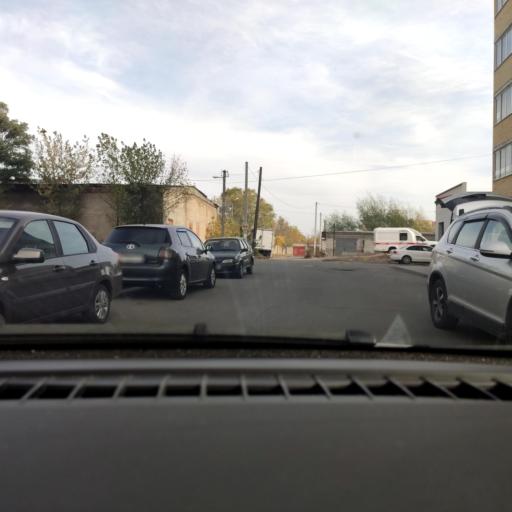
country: RU
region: Voronezj
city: Novaya Usman'
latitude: 51.6090
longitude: 39.3796
